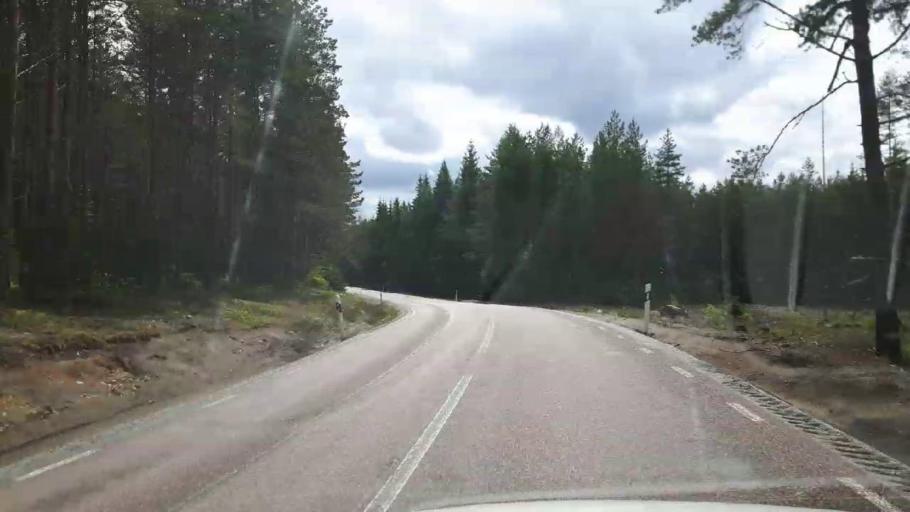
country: SE
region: Vaestmanland
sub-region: Fagersta Kommun
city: Fagersta
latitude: 59.9018
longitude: 15.8202
